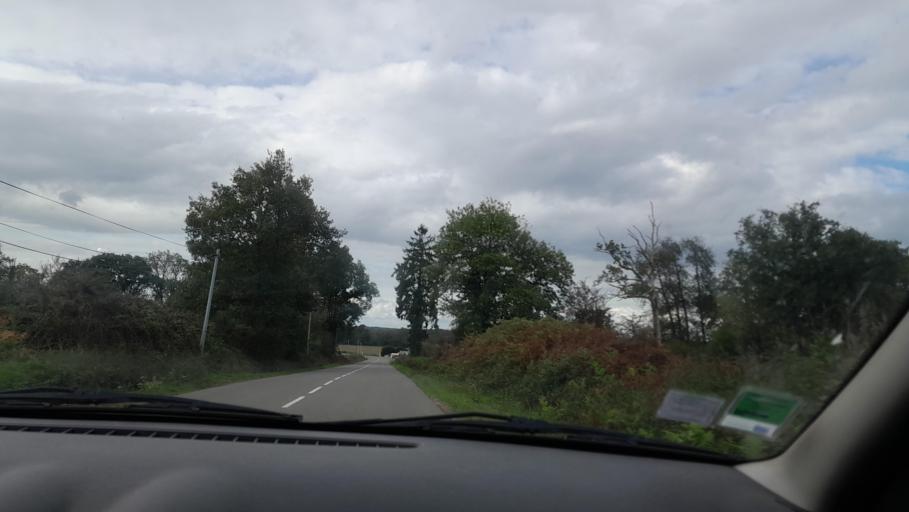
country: FR
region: Brittany
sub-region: Departement d'Ille-et-Vilaine
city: Argentre-du-Plessis
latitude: 48.0489
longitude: -1.0929
